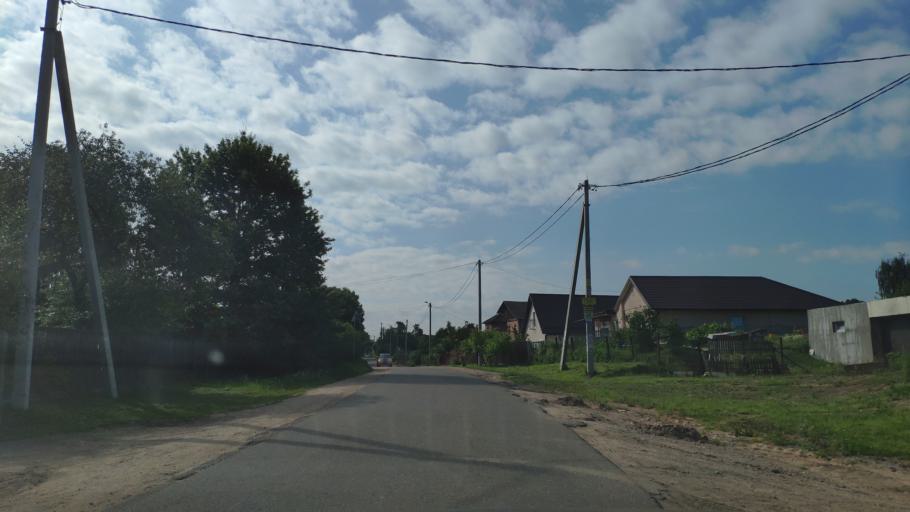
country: BY
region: Minsk
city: Zaslawye
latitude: 53.9990
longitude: 27.2803
